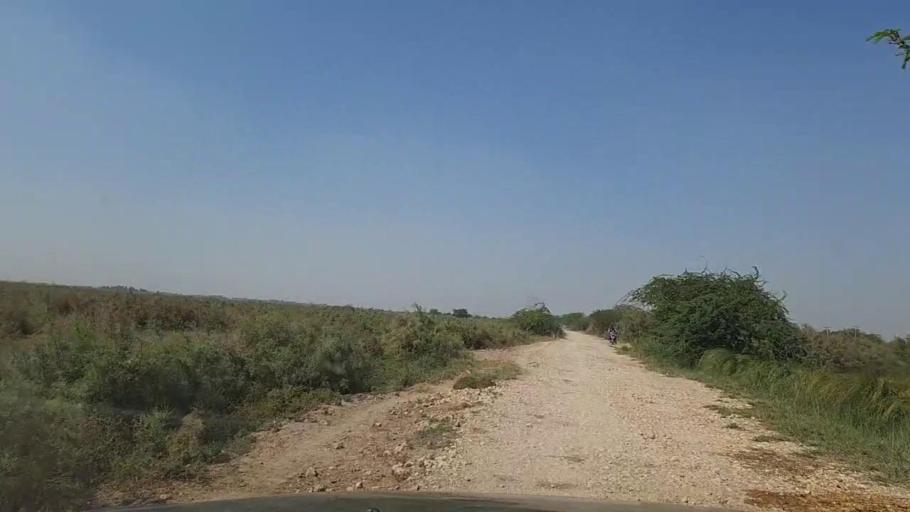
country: PK
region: Sindh
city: Daro Mehar
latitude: 24.8269
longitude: 68.1482
